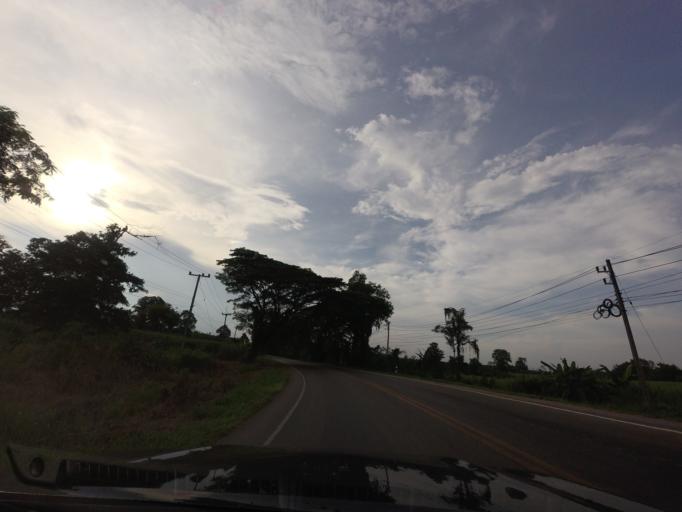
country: TH
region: Nong Khai
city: Pho Tak
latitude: 17.7830
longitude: 102.3763
